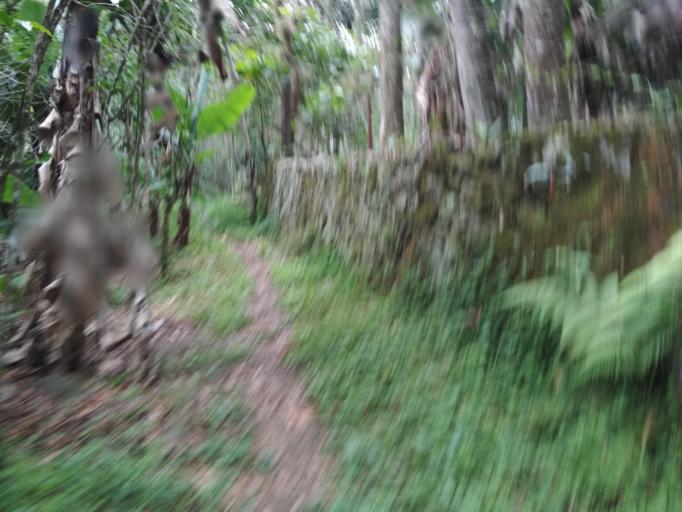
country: MX
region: Veracruz
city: Jilotepec
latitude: 19.6191
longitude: -96.9279
